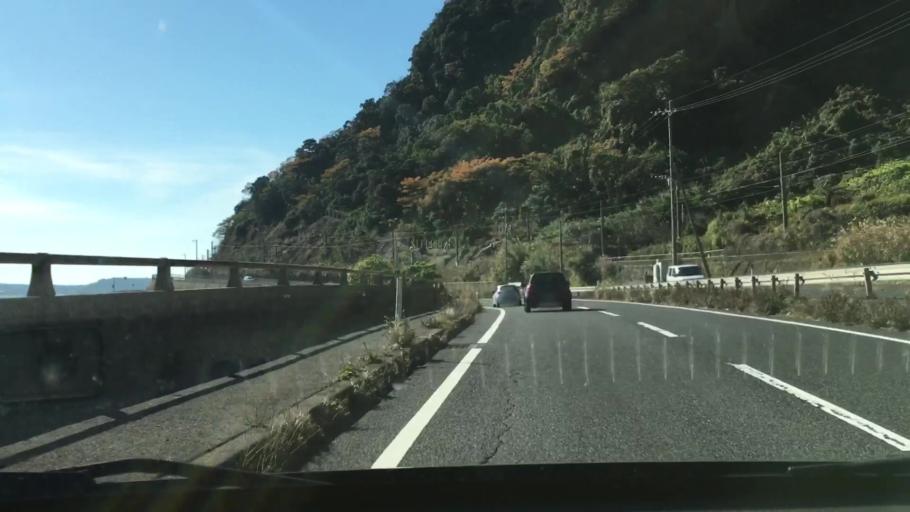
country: JP
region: Kagoshima
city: Kagoshima-shi
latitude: 31.6414
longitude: 130.6027
